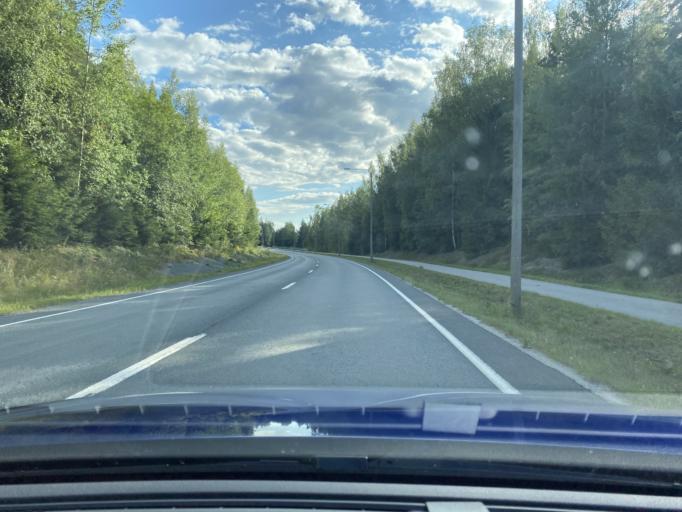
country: FI
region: Pirkanmaa
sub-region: Tampere
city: Lempaeaelae
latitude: 61.3711
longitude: 23.7839
